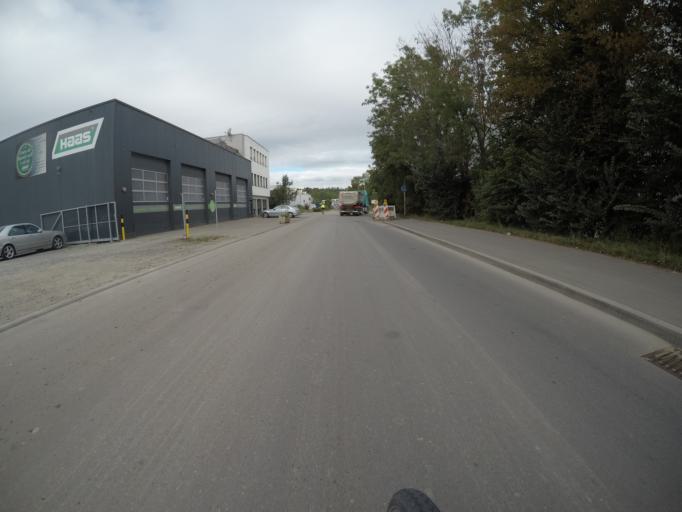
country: DE
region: Baden-Wuerttemberg
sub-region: Regierungsbezirk Stuttgart
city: Marbach am Neckar
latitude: 48.8906
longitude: 9.2655
